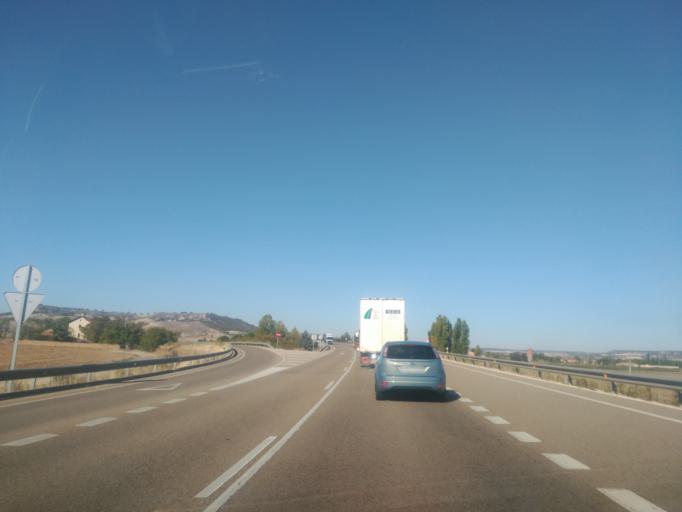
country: ES
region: Castille and Leon
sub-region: Provincia de Valladolid
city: Quintanilla de Arriba
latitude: 41.6178
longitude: -4.2052
